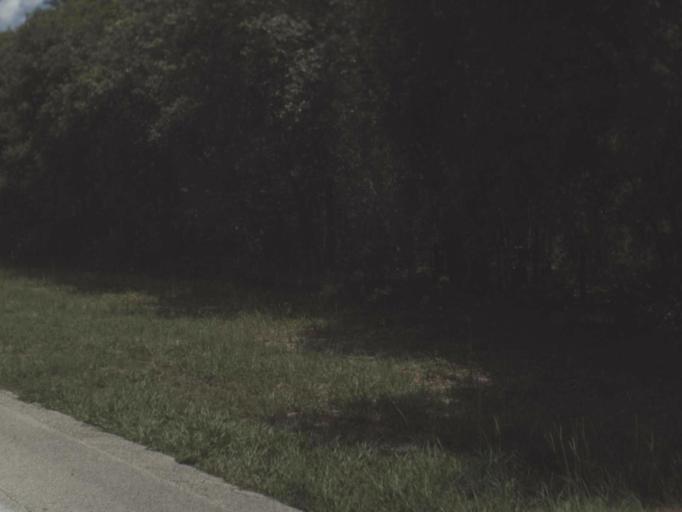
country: US
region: Florida
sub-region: Putnam County
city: Palatka
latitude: 29.5250
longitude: -81.6364
